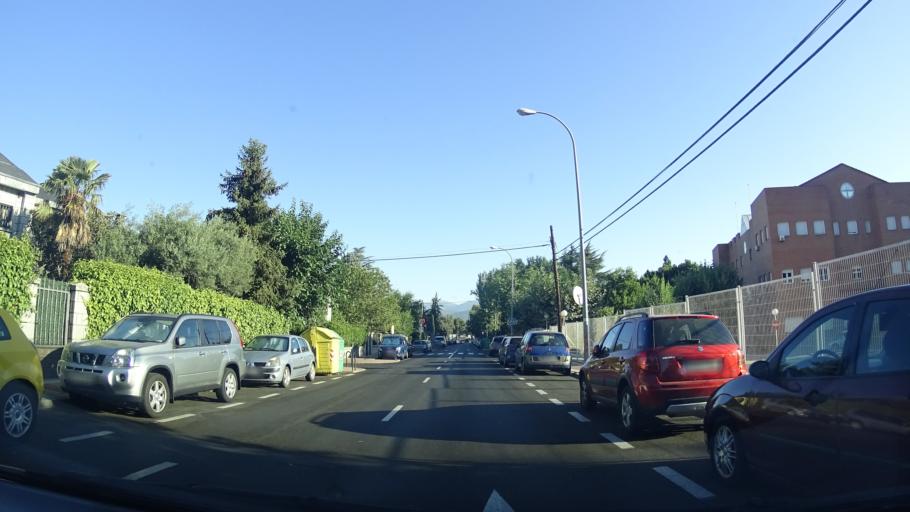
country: ES
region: Madrid
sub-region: Provincia de Madrid
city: Collado-Villalba
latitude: 40.6354
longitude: -4.0029
